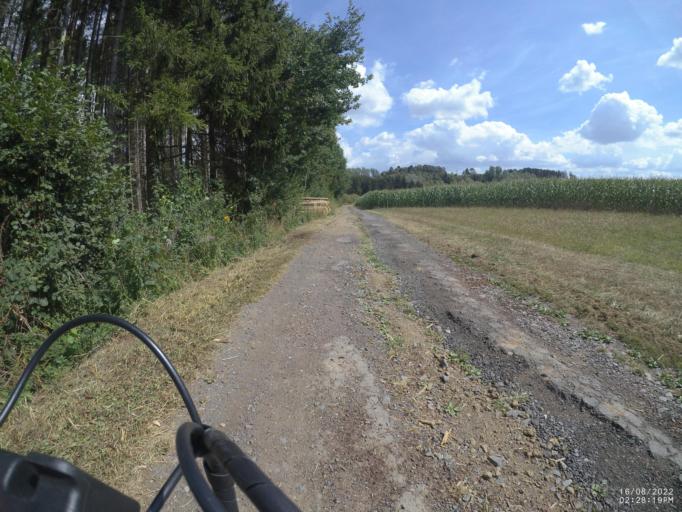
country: DE
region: Rheinland-Pfalz
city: Hillesheim
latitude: 50.3047
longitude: 6.6730
